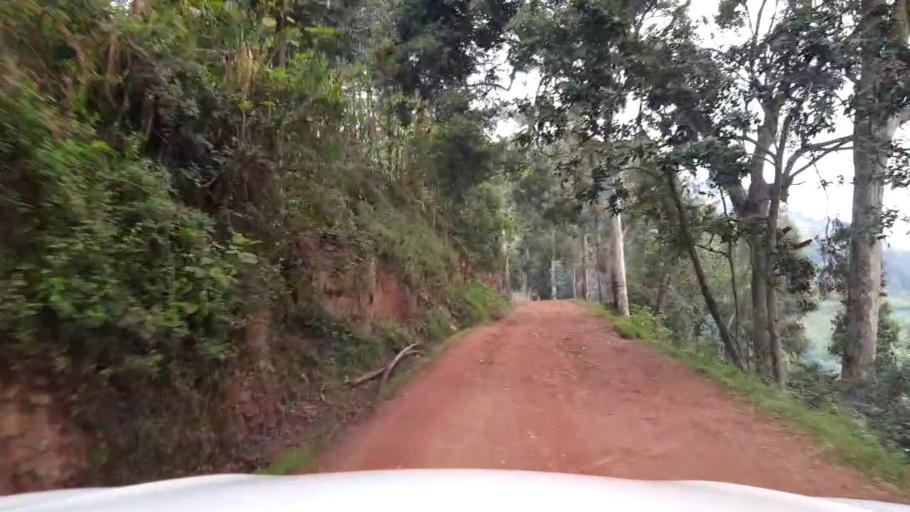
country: UG
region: Western Region
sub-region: Kisoro District
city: Kisoro
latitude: -1.3949
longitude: 29.8000
